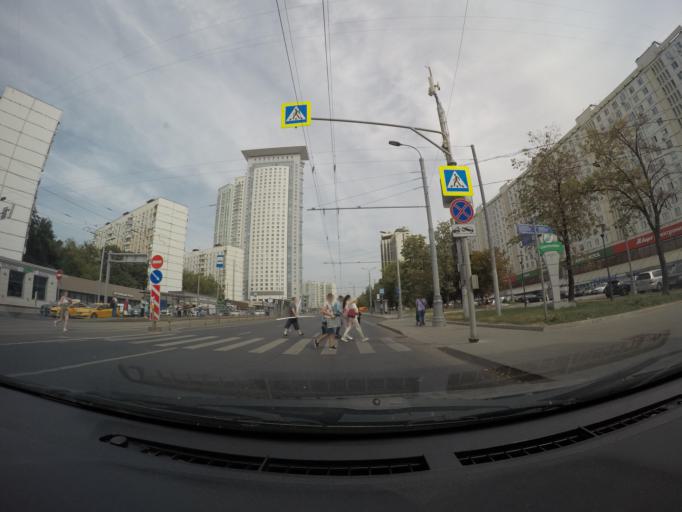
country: RU
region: Moscow
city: Sokol'niki
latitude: 55.7860
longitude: 37.6768
